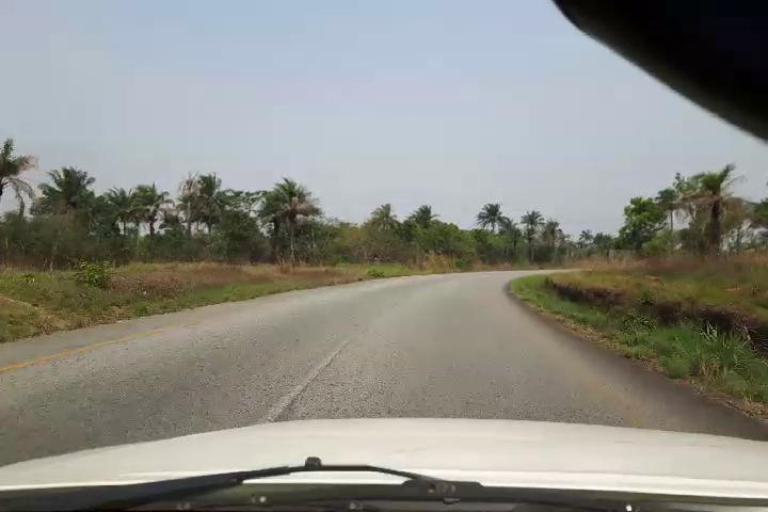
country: SL
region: Southern Province
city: Largo
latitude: 8.3043
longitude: -12.2030
